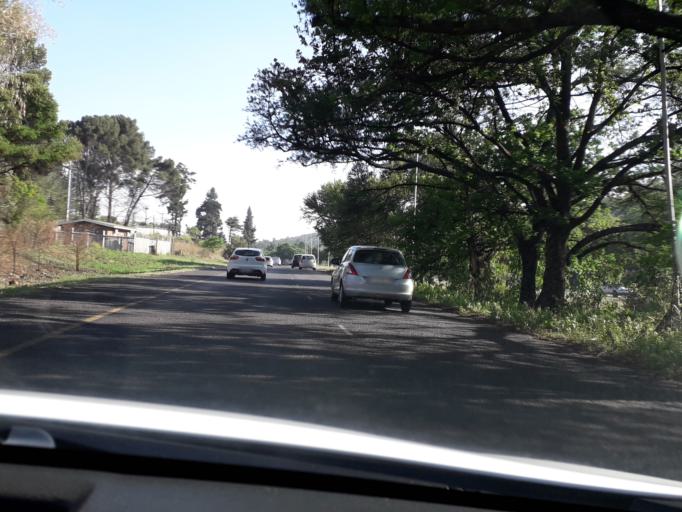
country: ZA
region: Gauteng
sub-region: City of Tshwane Metropolitan Municipality
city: Pretoria
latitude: -25.7948
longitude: 28.1959
